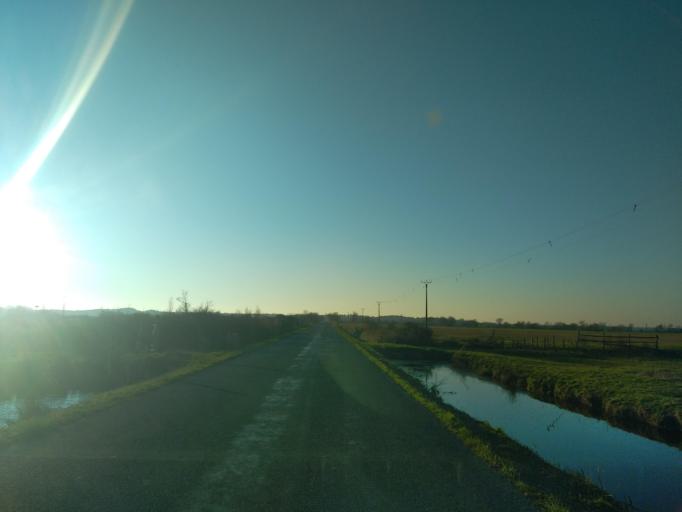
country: FR
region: Pays de la Loire
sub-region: Departement de la Vendee
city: Angles
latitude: 46.3887
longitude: -1.4442
